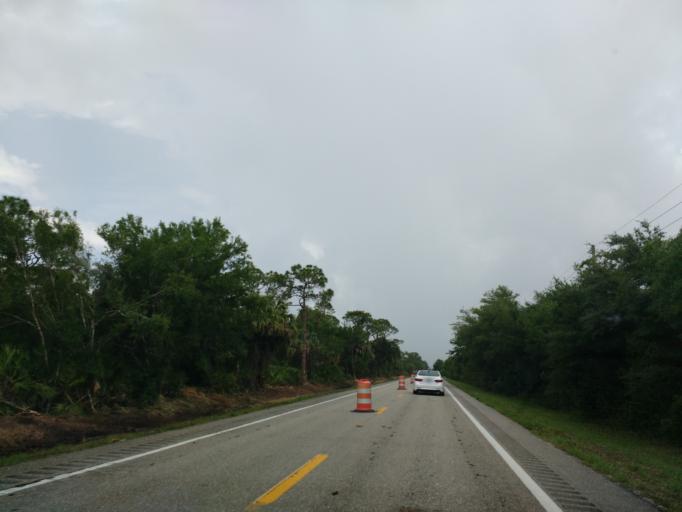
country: US
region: Florida
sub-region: Lee County
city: Burnt Store Marina
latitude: 26.8354
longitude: -82.0215
